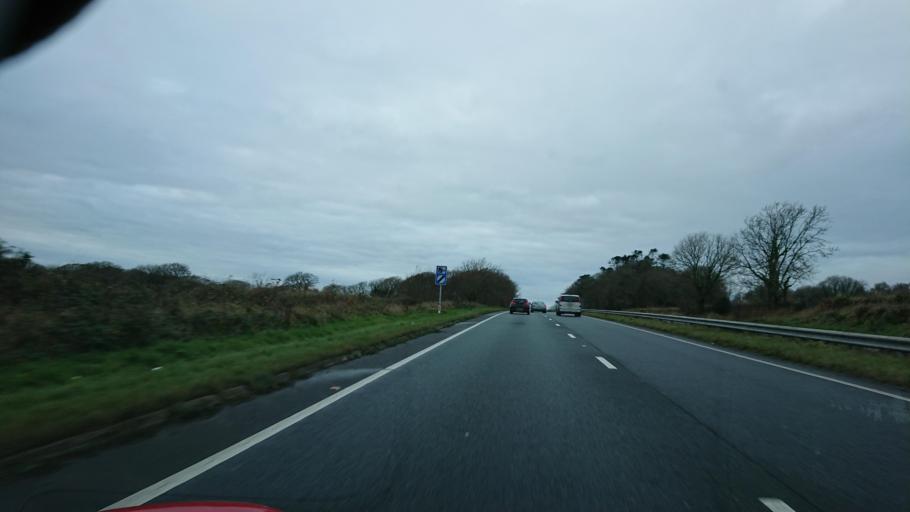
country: GB
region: England
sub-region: Cornwall
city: Liskeard
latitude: 50.4247
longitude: -4.4159
